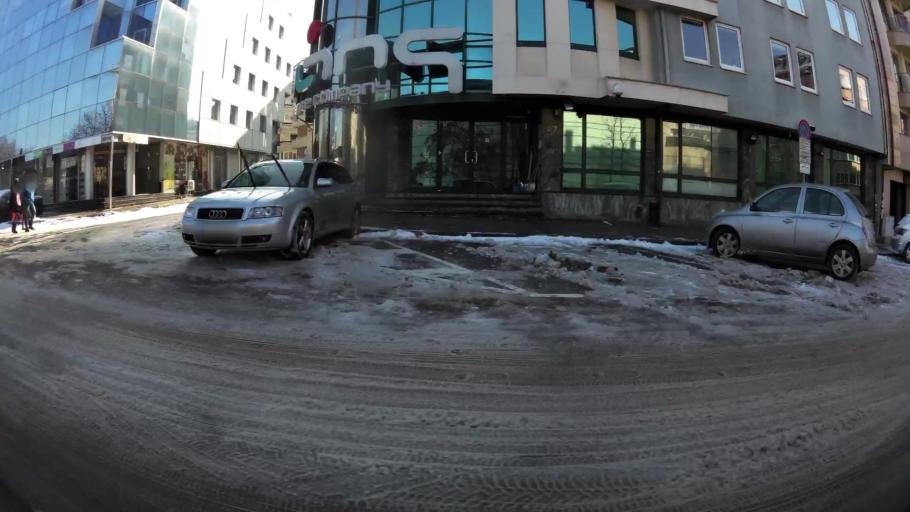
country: BG
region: Sofia-Capital
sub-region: Stolichna Obshtina
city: Sofia
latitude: 42.6709
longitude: 23.3161
